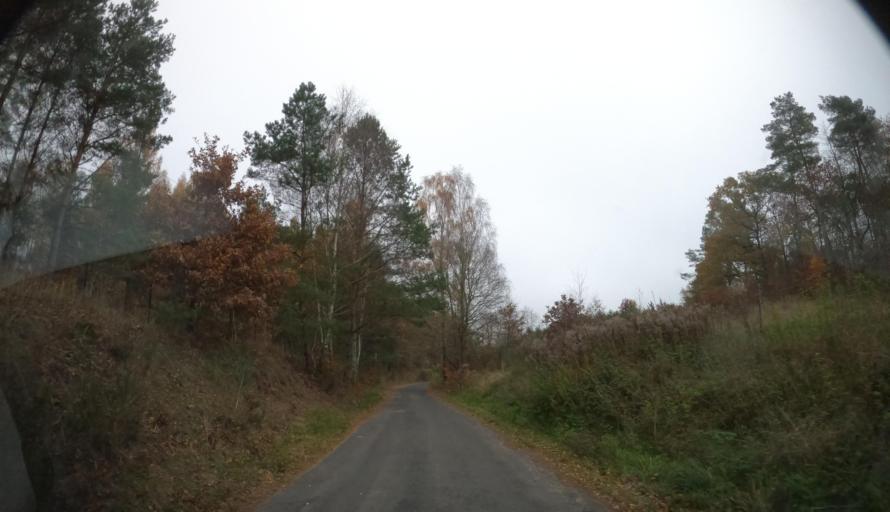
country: PL
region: West Pomeranian Voivodeship
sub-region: Powiat lobeski
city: Radowo Male
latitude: 53.6828
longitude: 15.4559
